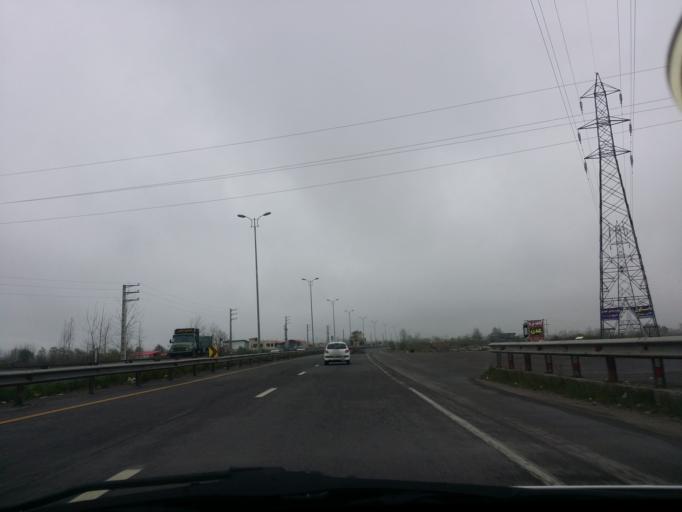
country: IR
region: Mazandaran
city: Tonekabon
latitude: 36.7966
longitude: 50.9013
